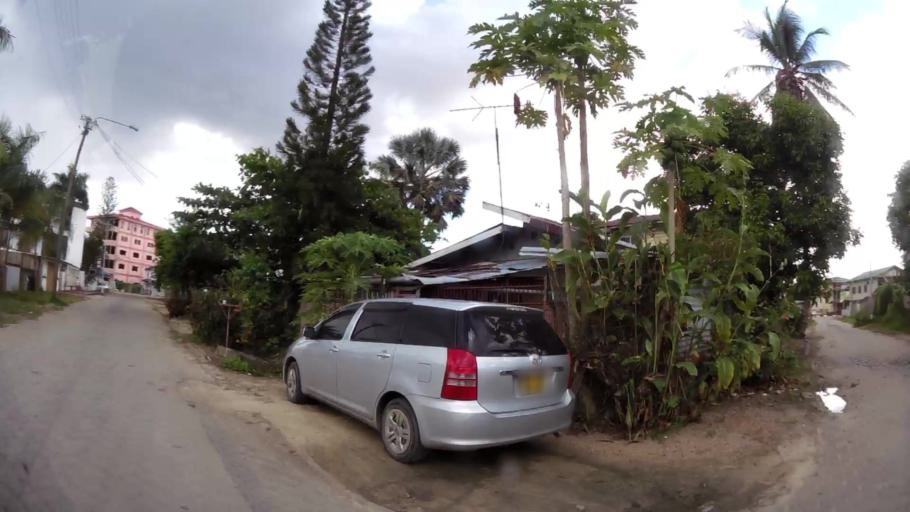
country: SR
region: Paramaribo
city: Paramaribo
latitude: 5.8291
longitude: -55.1486
